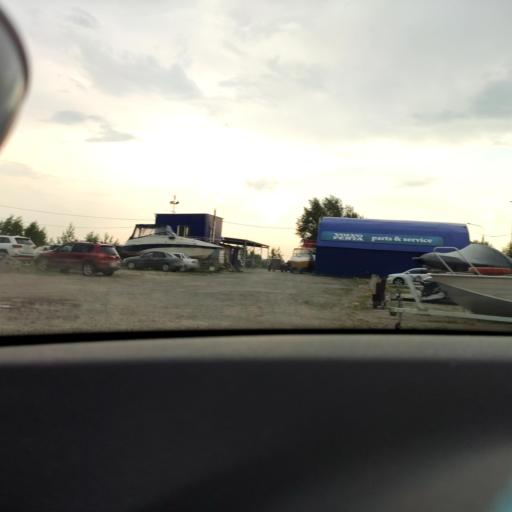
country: RU
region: Samara
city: Samara
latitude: 53.1747
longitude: 50.1230
